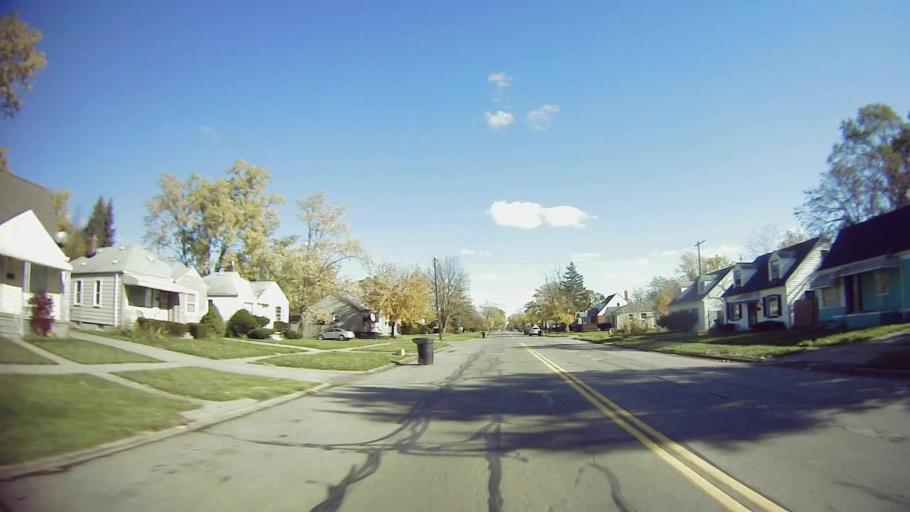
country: US
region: Michigan
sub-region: Wayne County
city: Dearborn Heights
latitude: 42.3502
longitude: -83.2427
